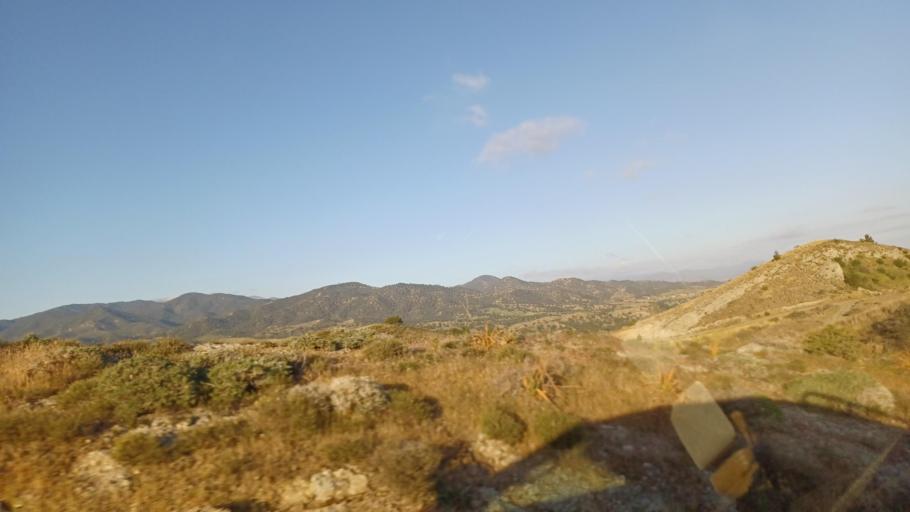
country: CY
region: Lefkosia
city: Astromeritis
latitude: 35.0683
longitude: 33.0363
